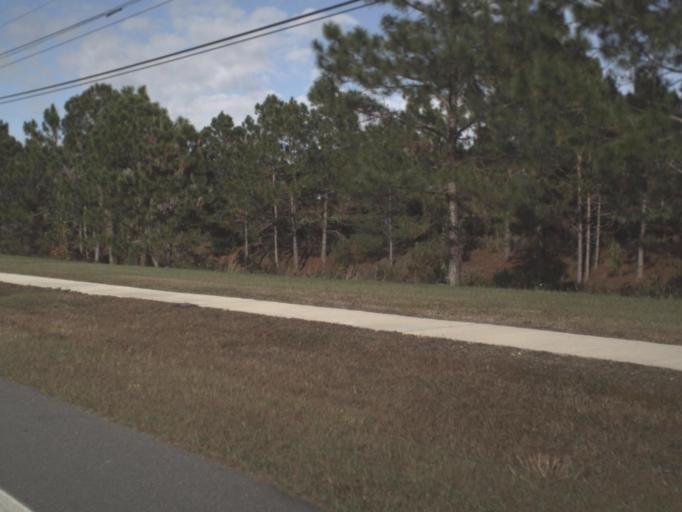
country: US
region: Florida
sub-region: Volusia County
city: Holly Hill
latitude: 29.2191
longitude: -81.0920
